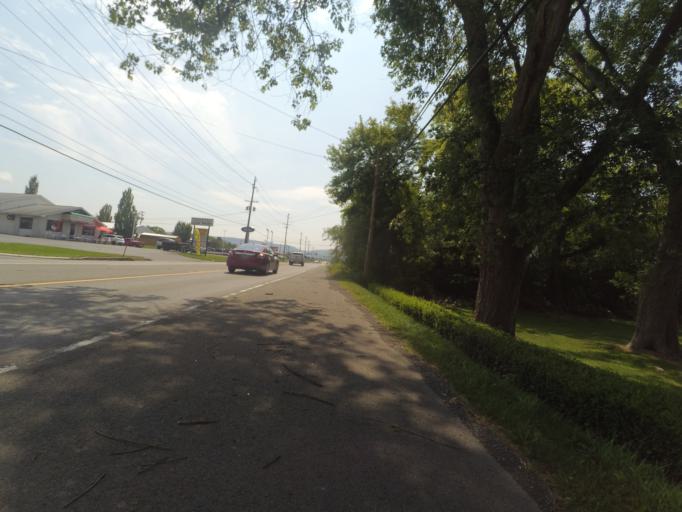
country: US
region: Pennsylvania
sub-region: Centre County
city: Bellefonte
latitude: 40.8864
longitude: -77.7815
